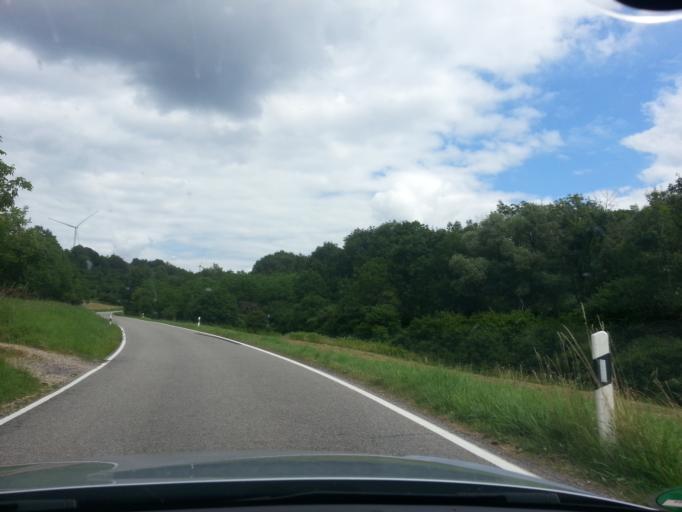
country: DE
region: Saarland
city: Beckingen
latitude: 49.4373
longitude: 6.6910
